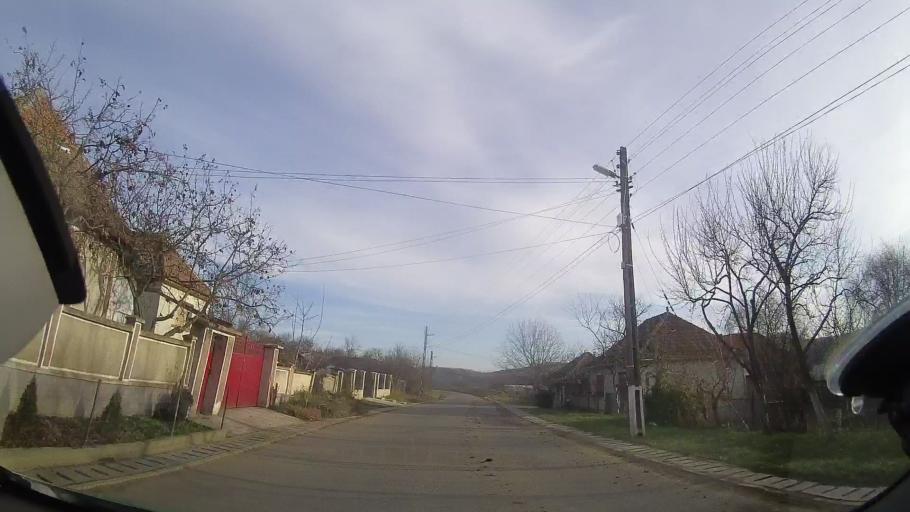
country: RO
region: Bihor
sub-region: Comuna Sarbi
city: Burzuc
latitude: 47.1474
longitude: 22.1798
